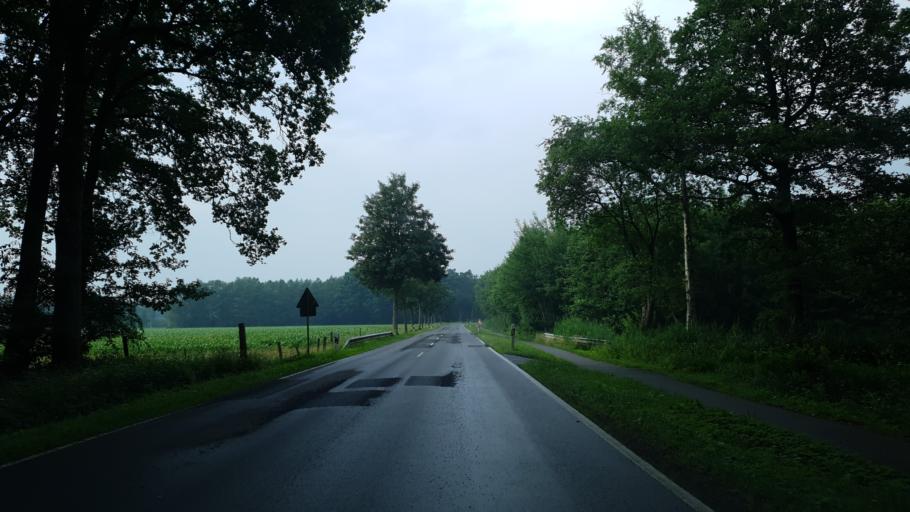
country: DE
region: Lower Saxony
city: Meppen
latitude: 52.6624
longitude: 7.3143
